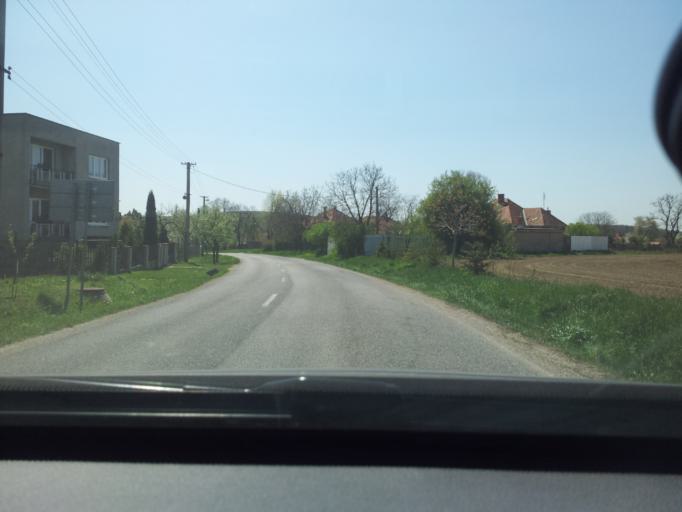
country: SK
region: Nitriansky
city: Zlate Moravce
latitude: 48.3103
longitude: 18.4444
